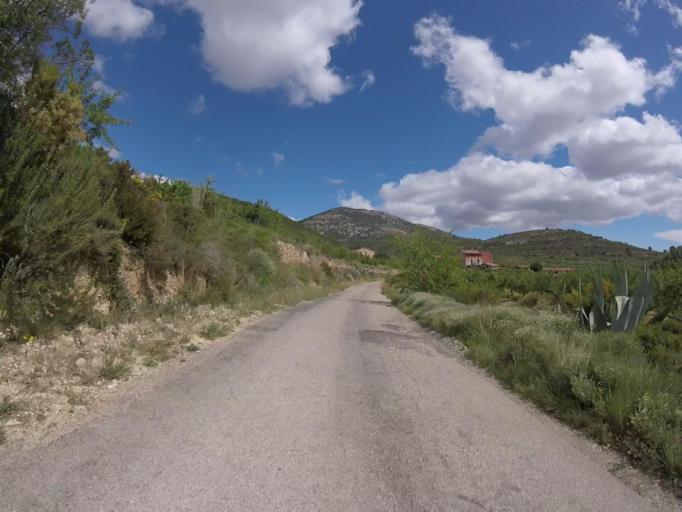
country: ES
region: Valencia
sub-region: Provincia de Castello
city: Sierra-Engarceran
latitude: 40.2732
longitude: -0.0910
